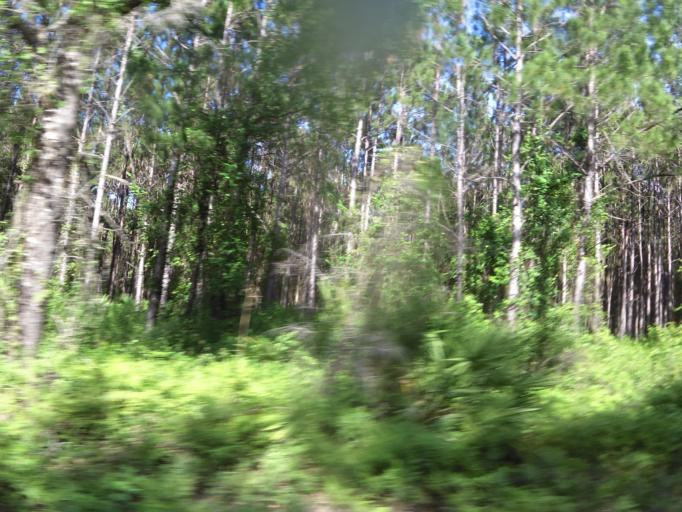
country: US
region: Florida
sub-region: Nassau County
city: Callahan
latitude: 30.5691
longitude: -81.7811
